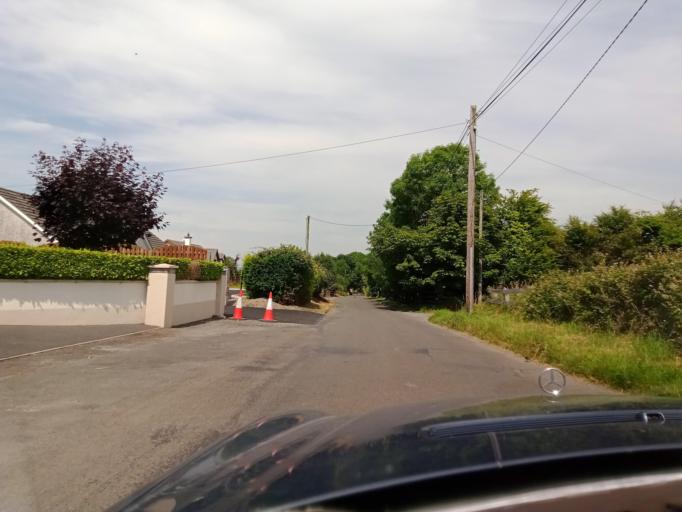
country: IE
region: Leinster
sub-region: Kilkenny
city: Mooncoin
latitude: 52.2725
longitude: -7.2166
